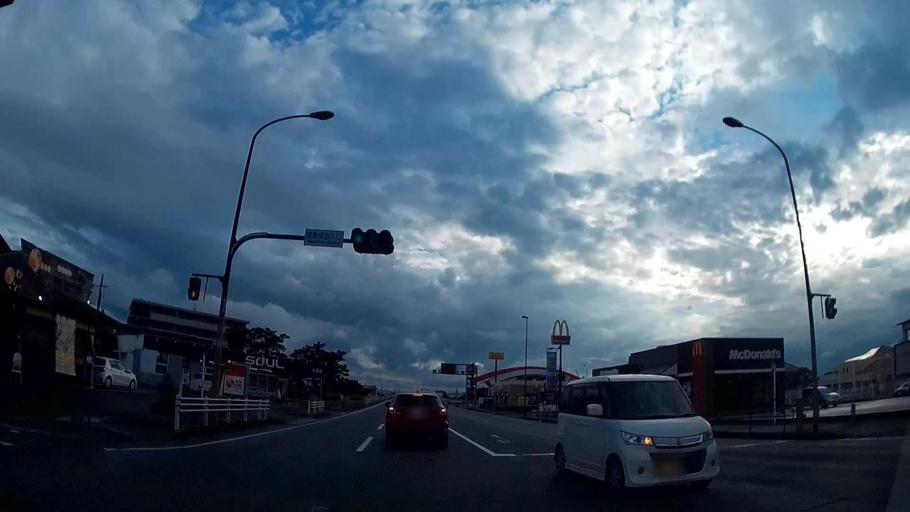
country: JP
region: Kumamoto
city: Ozu
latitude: 32.8784
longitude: 130.8865
